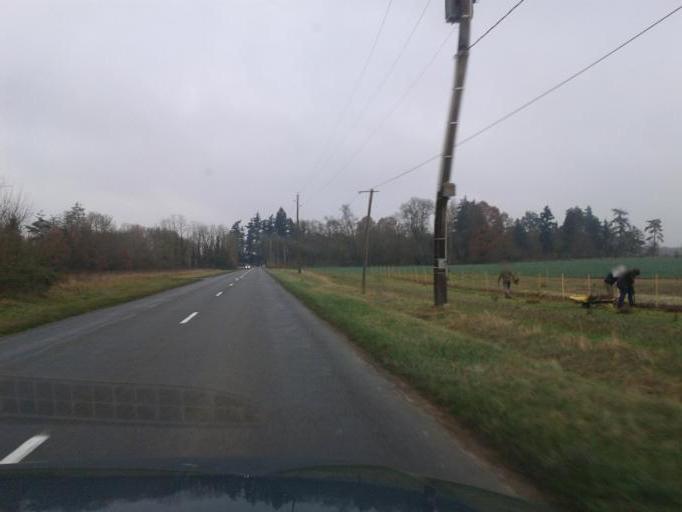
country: FR
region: Centre
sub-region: Departement du Loiret
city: Beaugency
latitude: 47.7606
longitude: 1.6426
